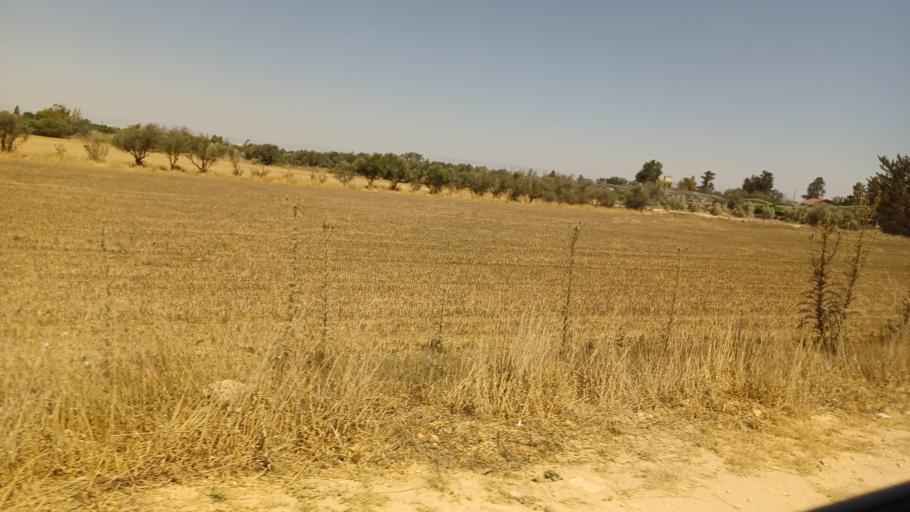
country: CY
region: Ammochostos
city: Frenaros
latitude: 35.0696
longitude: 33.8953
